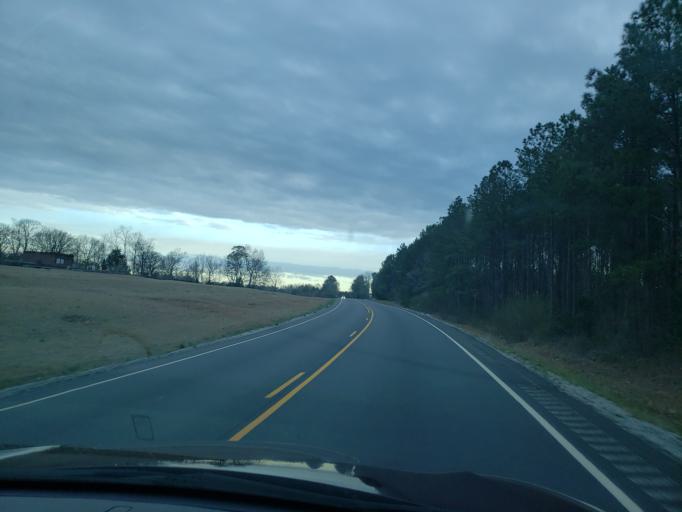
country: US
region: Alabama
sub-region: Randolph County
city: Roanoke
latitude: 33.0659
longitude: -85.3328
